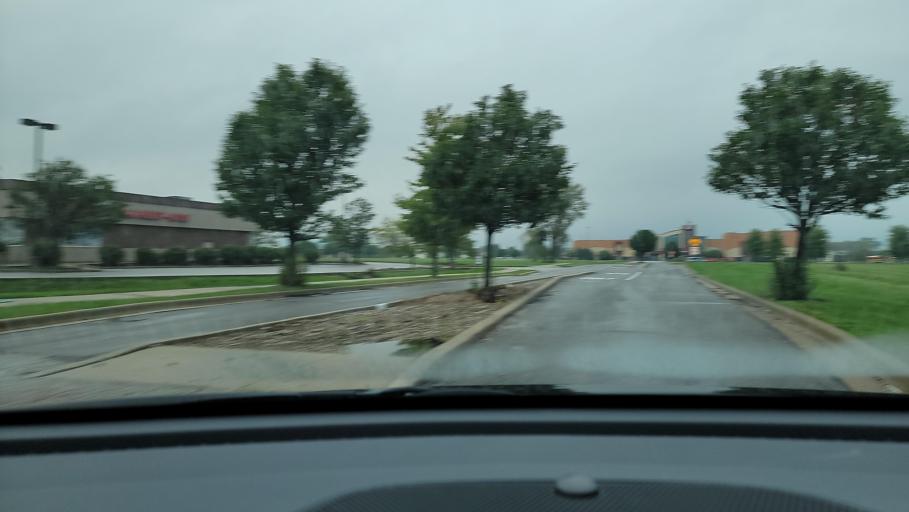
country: US
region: Indiana
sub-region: Porter County
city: South Haven
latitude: 41.5506
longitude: -87.1602
